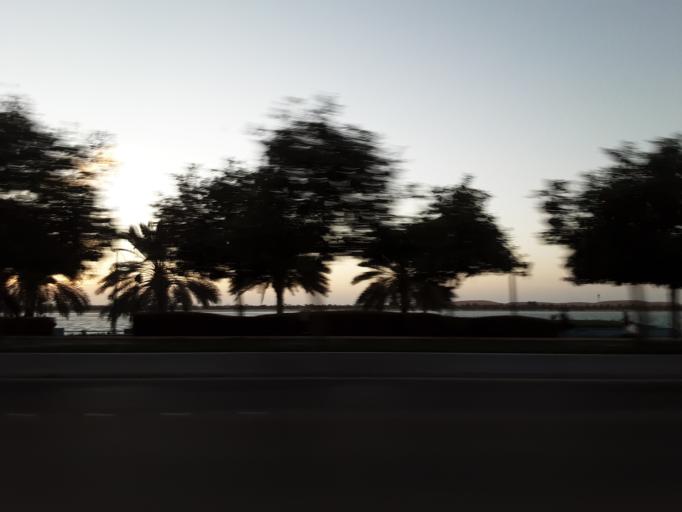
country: AE
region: Abu Dhabi
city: Abu Dhabi
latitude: 24.4925
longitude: 54.3543
